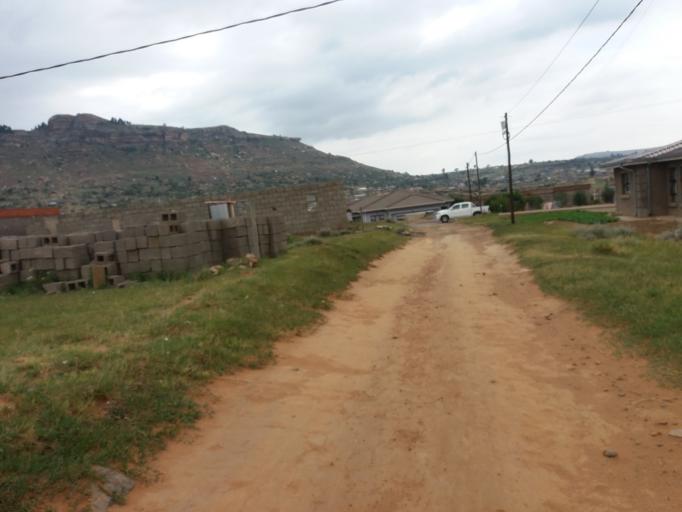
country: LS
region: Maseru
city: Maseru
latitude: -29.3673
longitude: 27.4756
